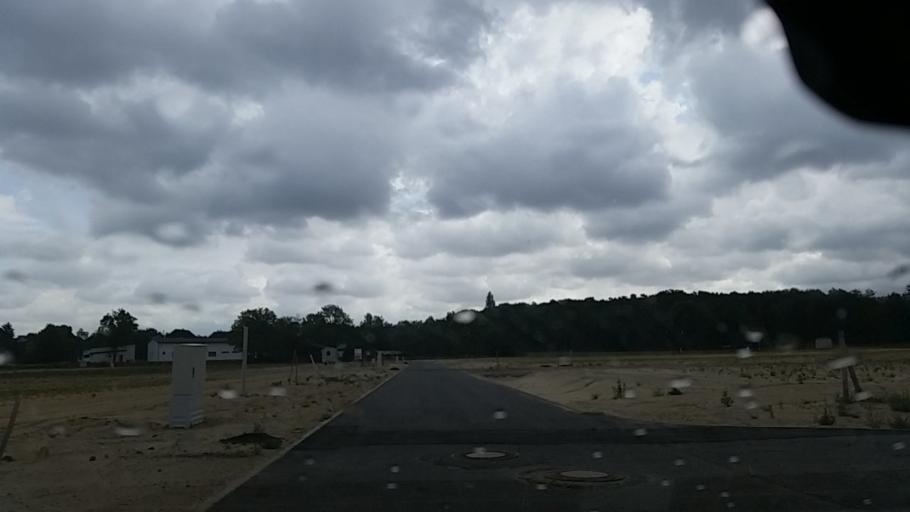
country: DE
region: Lower Saxony
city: Wolfsburg
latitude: 52.4245
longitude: 10.8323
